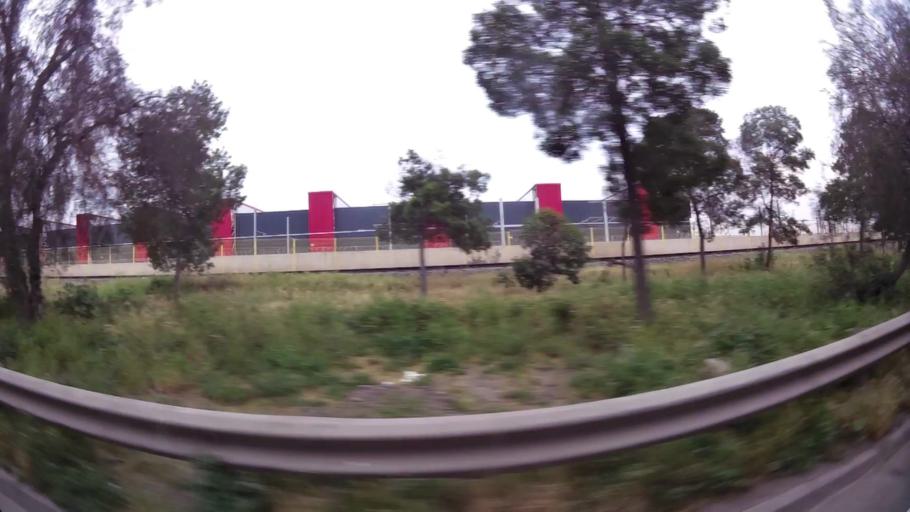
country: CL
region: Santiago Metropolitan
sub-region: Provincia de Santiago
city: Lo Prado
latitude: -33.4834
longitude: -70.7071
